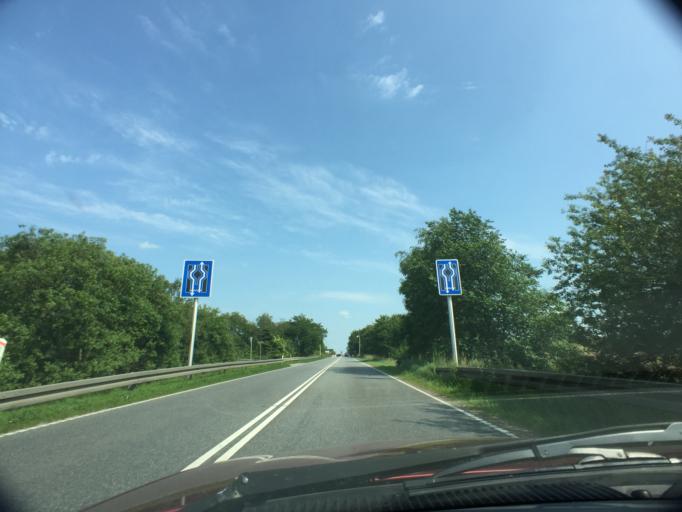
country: DK
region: Central Jutland
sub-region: Favrskov Kommune
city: Hammel
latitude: 56.2398
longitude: 9.8086
